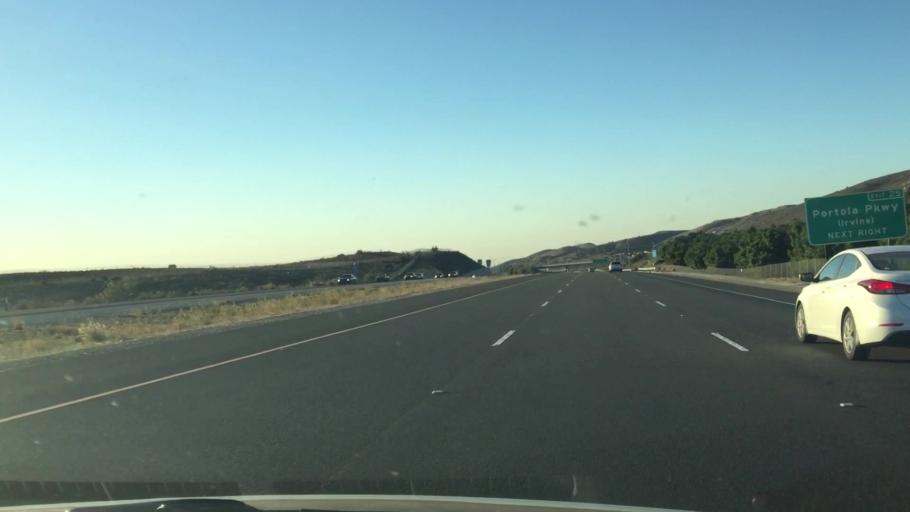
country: US
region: California
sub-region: Orange County
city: Foothill Ranch
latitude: 33.6892
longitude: -117.6829
